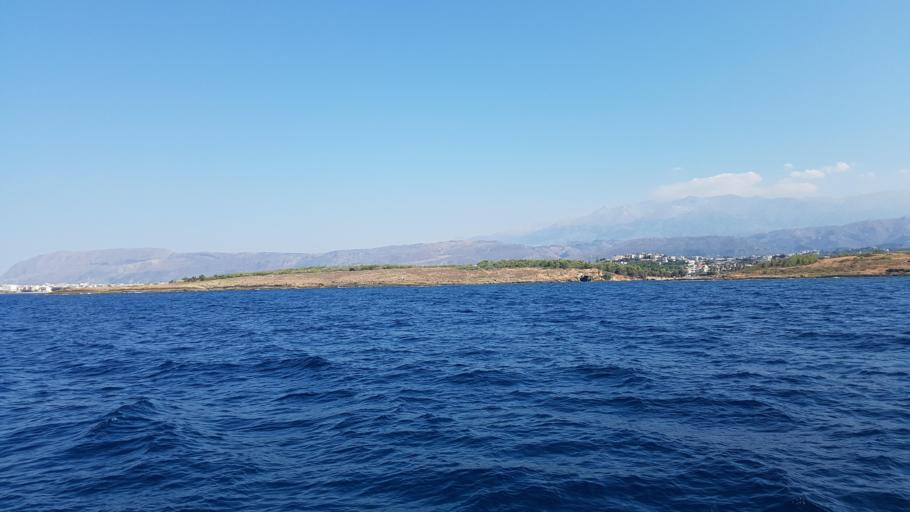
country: GR
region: Crete
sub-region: Nomos Chanias
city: Daratsos
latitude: 35.5218
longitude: 23.9814
